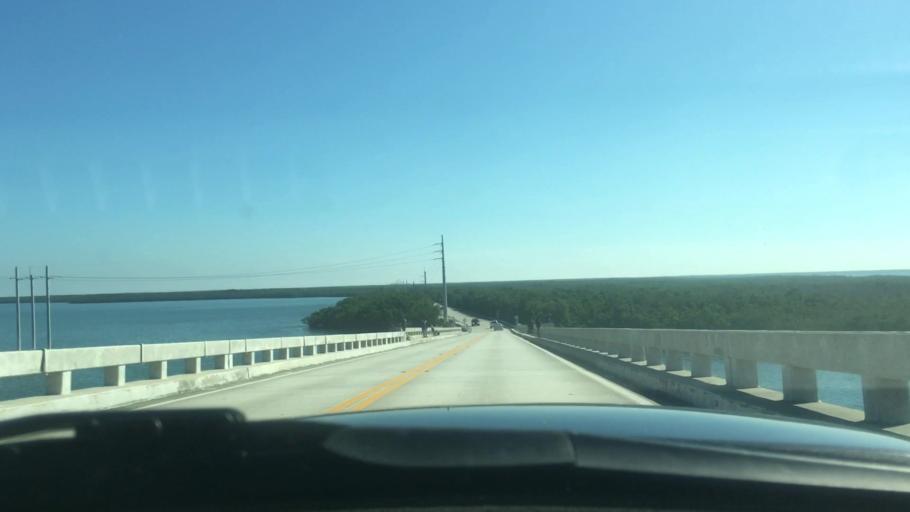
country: US
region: Florida
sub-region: Monroe County
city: North Key Largo
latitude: 25.2863
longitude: -80.3663
